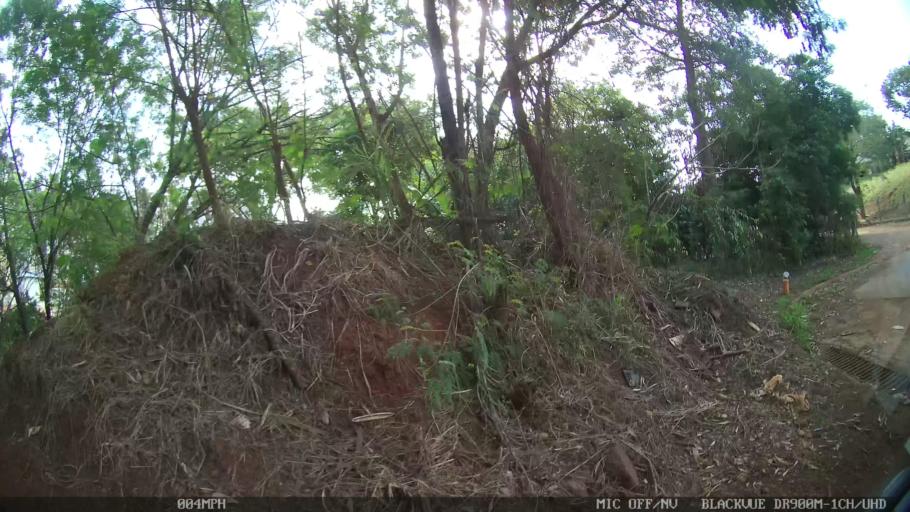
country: BR
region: Sao Paulo
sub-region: Paulinia
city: Paulinia
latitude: -22.7560
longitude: -47.1487
